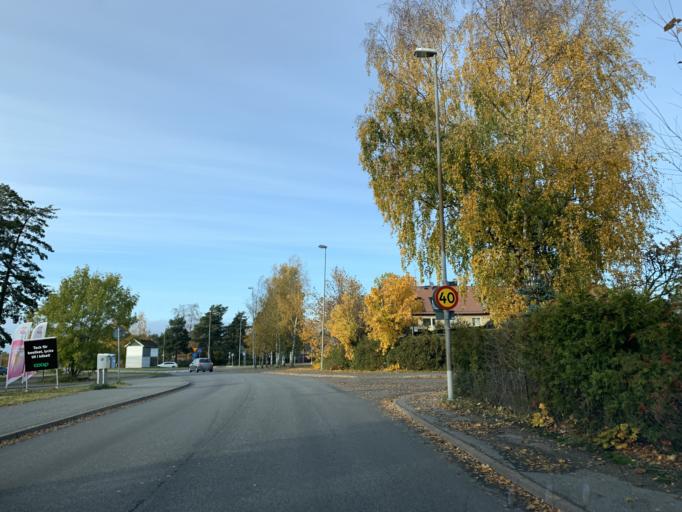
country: SE
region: Stockholm
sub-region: Haninge Kommun
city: Haninge
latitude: 59.1798
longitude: 18.1813
